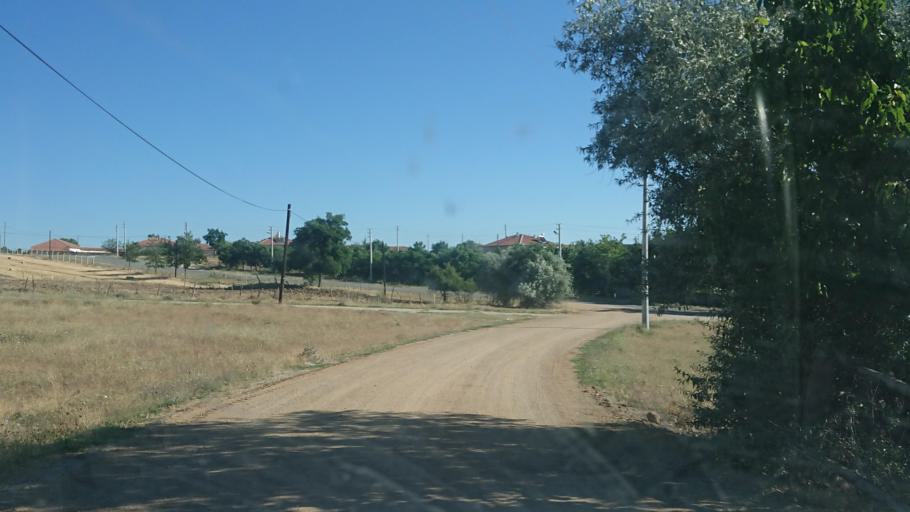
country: TR
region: Aksaray
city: Agacoren
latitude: 38.8765
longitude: 33.9522
